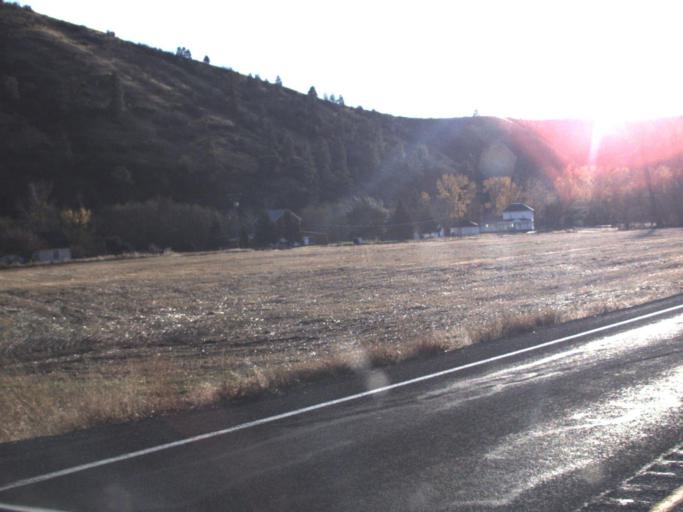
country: US
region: Washington
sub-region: Walla Walla County
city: Waitsburg
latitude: 46.2726
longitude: -118.1274
